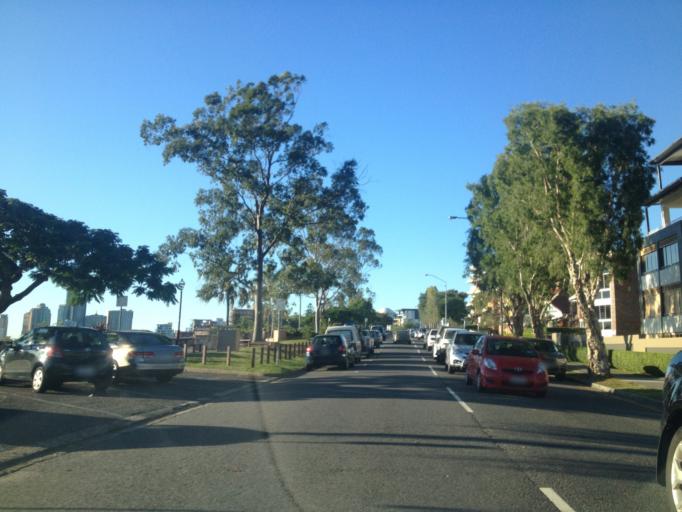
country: AU
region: Queensland
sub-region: Brisbane
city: Woolloongabba
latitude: -27.4793
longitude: 153.0341
